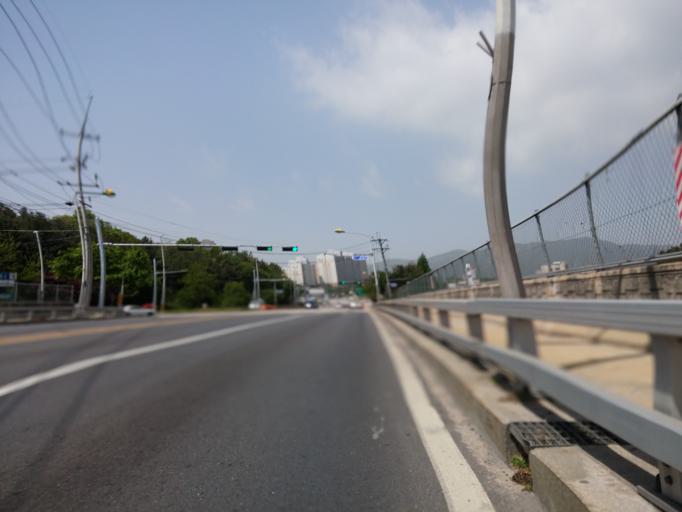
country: KR
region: Chungcheongnam-do
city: Nonsan
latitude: 36.2825
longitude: 127.2452
